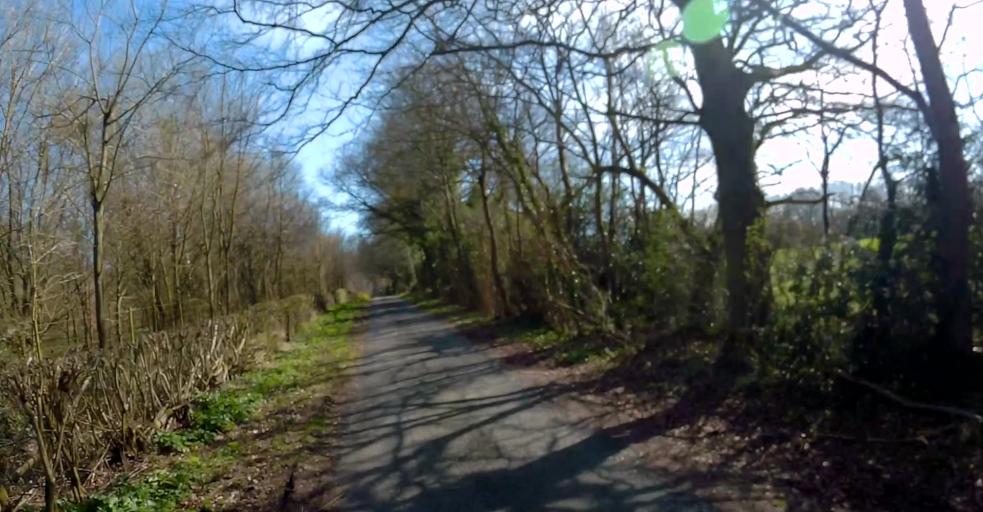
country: GB
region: England
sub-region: Hampshire
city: Four Marks
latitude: 51.1774
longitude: -1.0644
